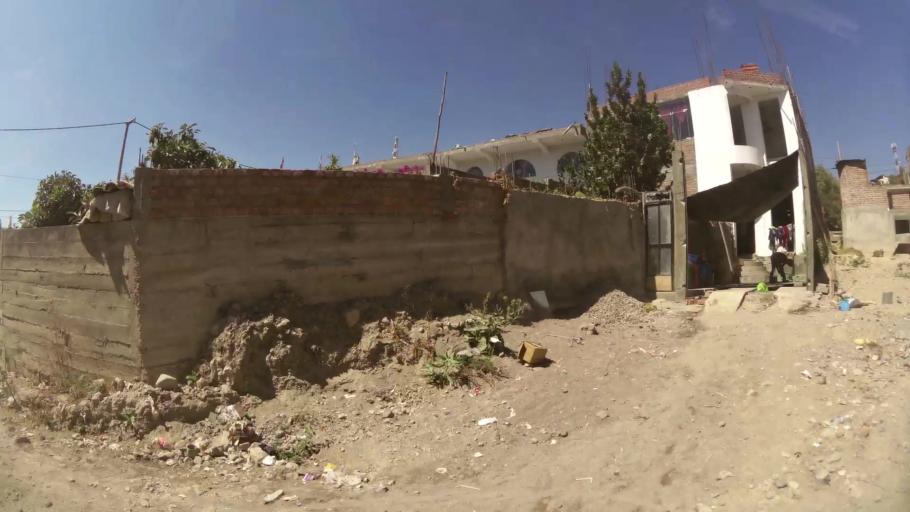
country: PE
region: Ayacucho
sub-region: Provincia de Huamanga
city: Ayacucho
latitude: -13.1682
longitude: -74.2311
